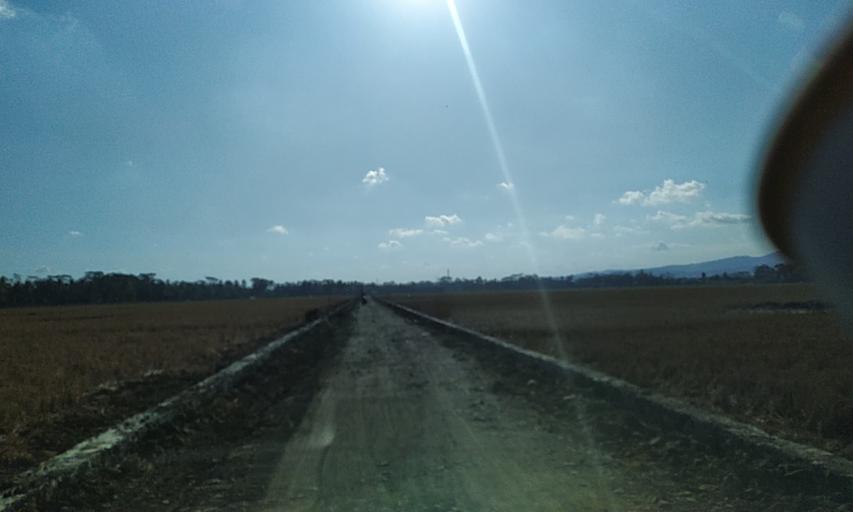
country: ID
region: Central Java
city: Krikil
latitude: -7.6238
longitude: 109.1380
